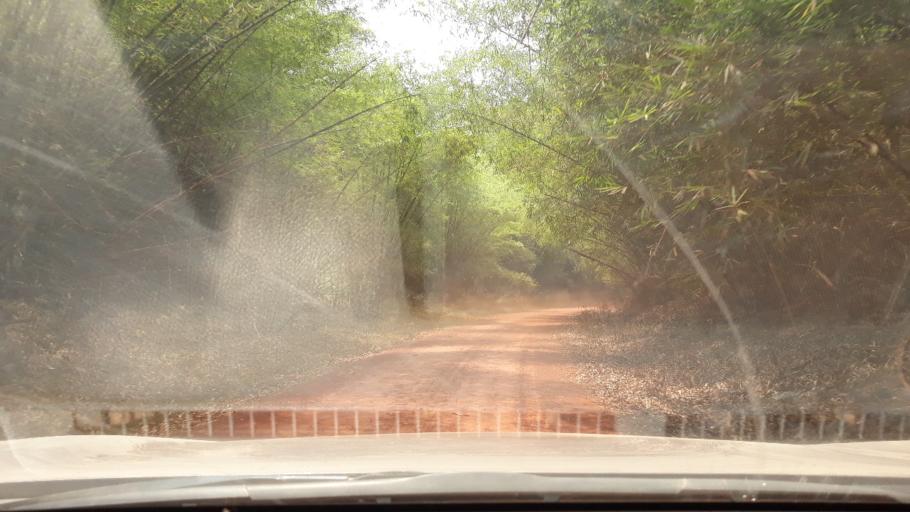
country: CD
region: Eastern Province
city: Buta
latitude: 2.3012
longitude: 25.0301
